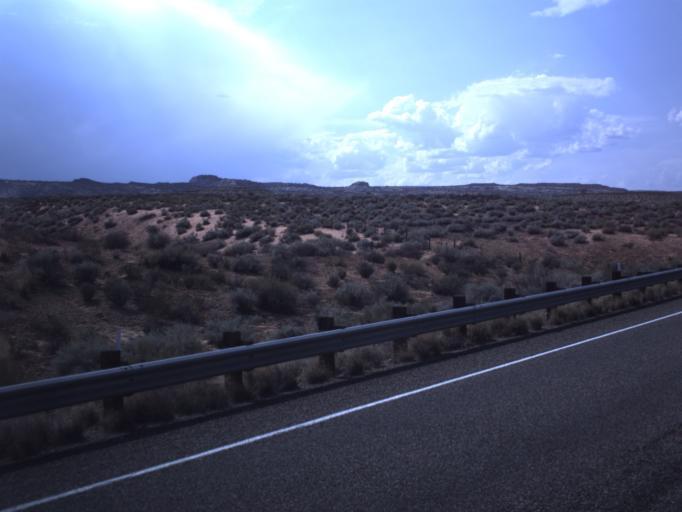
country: US
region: Arizona
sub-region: Coconino County
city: Page
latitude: 37.0521
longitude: -111.6300
